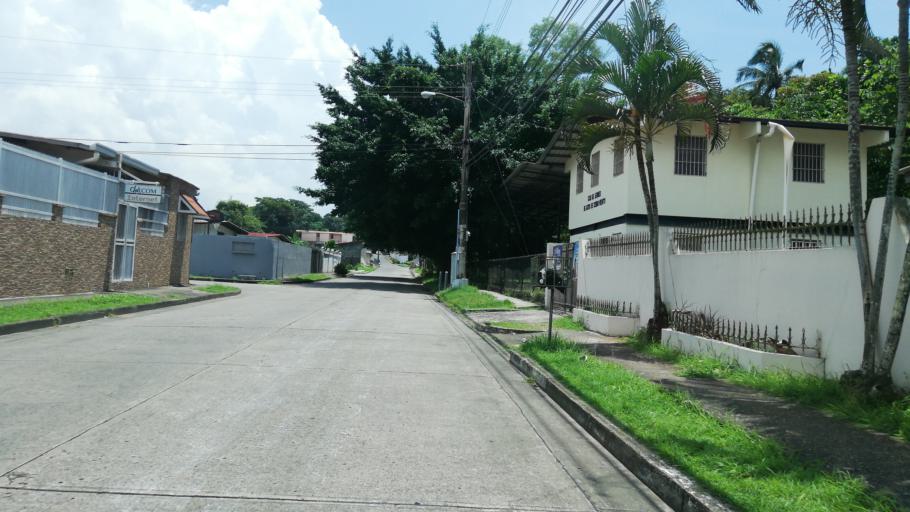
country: PA
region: Panama
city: San Miguelito
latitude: 9.0613
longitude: -79.4548
